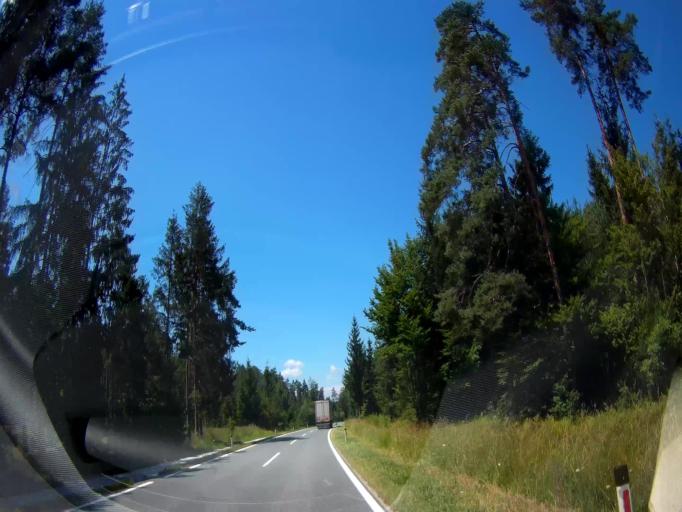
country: AT
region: Carinthia
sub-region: Politischer Bezirk Volkermarkt
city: Eberndorf
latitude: 46.6168
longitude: 14.6584
